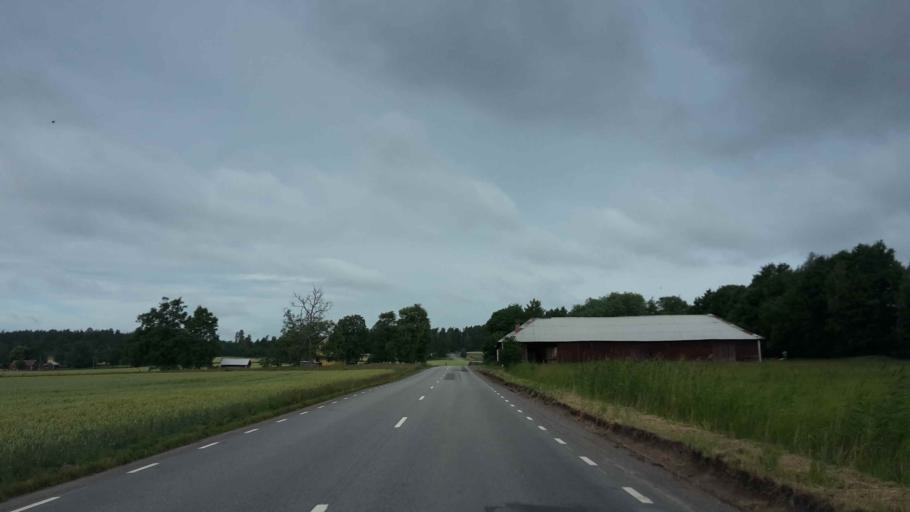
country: SE
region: OEstergoetland
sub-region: Motala Kommun
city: Motala
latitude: 58.5878
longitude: 15.0027
